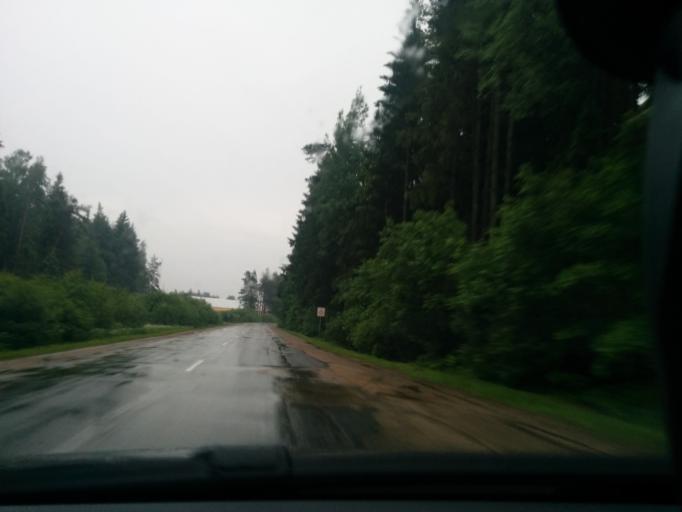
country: LV
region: Ogre
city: Ogre
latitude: 56.8280
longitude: 24.5948
